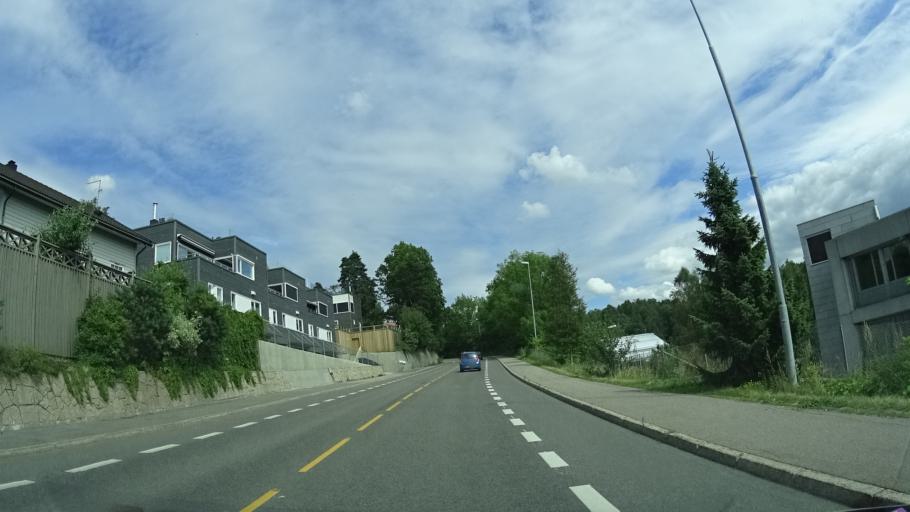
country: NO
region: Oslo
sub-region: Oslo
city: Oslo
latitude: 59.9549
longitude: 10.7615
